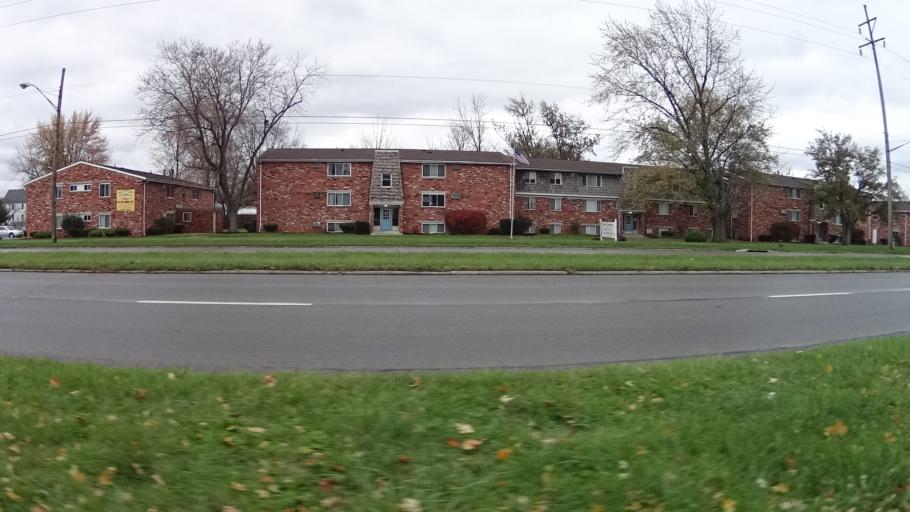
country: US
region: Ohio
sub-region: Lorain County
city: Elyria
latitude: 41.3798
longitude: -82.1172
